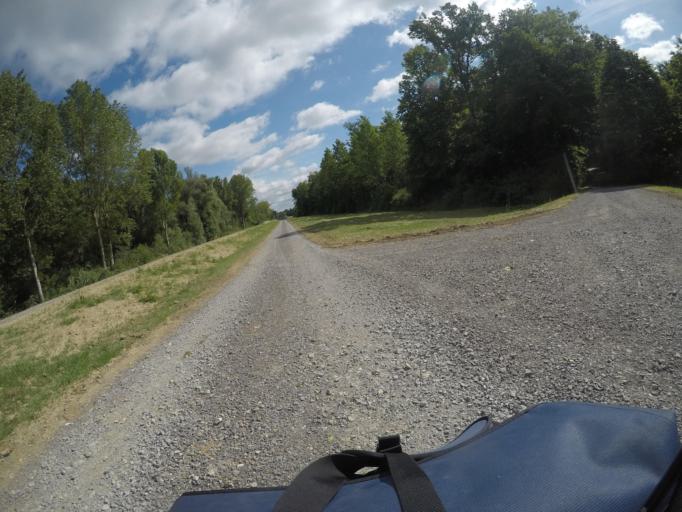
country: DE
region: Baden-Wuerttemberg
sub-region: Karlsruhe Region
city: Au am Rhein
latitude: 48.9437
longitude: 8.2046
